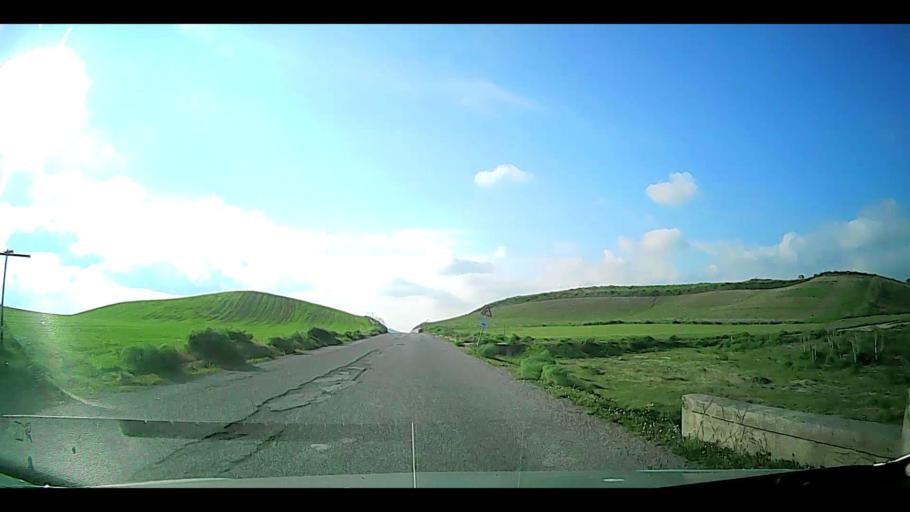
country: IT
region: Calabria
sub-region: Provincia di Crotone
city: Rocca di Neto
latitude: 39.1933
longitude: 17.0589
